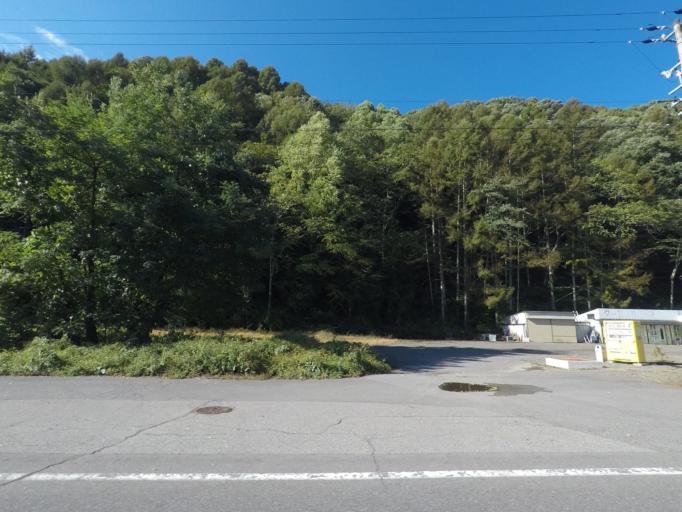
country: JP
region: Nagano
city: Ina
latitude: 35.9564
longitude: 137.7689
